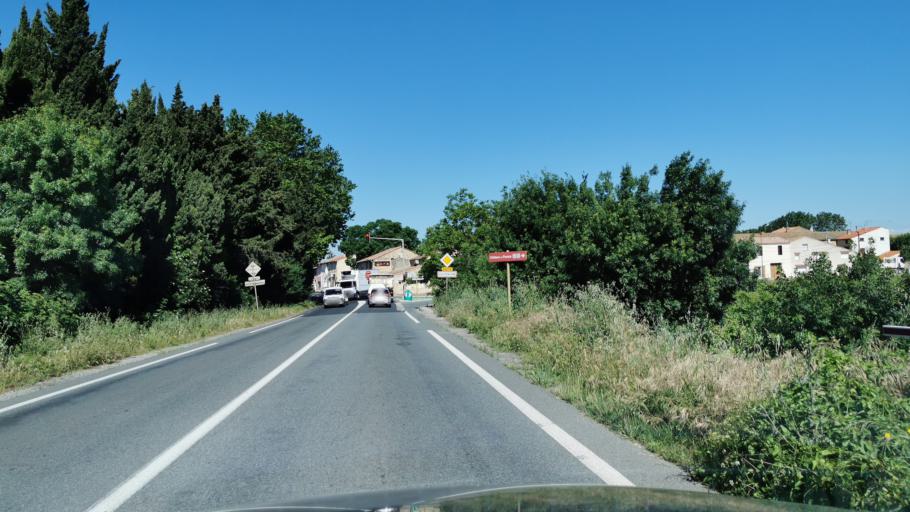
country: FR
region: Languedoc-Roussillon
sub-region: Departement de l'Aude
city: Canet
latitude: 43.2139
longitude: 2.8640
